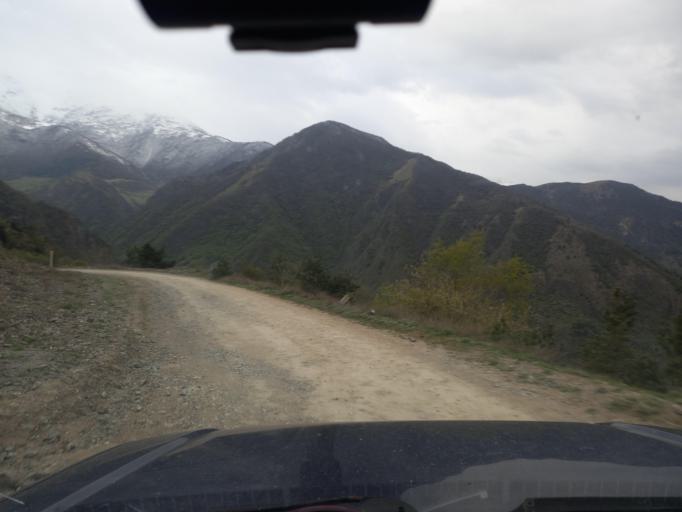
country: RU
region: North Ossetia
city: Mizur
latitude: 42.8558
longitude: 44.1644
